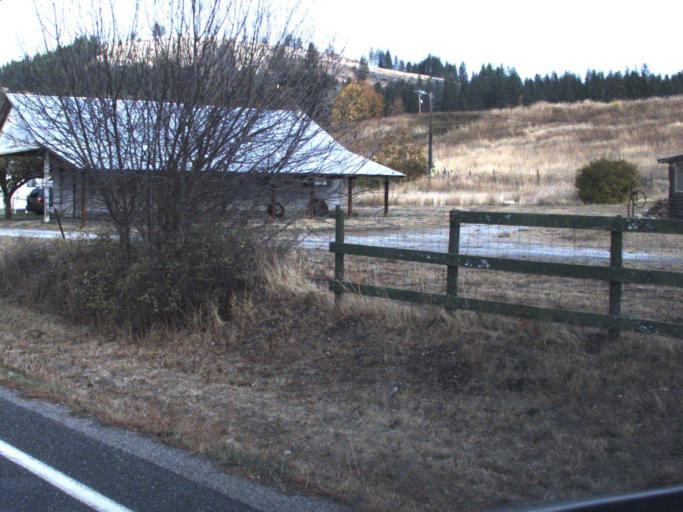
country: US
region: Washington
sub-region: Stevens County
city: Kettle Falls
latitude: 48.7508
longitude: -118.0453
